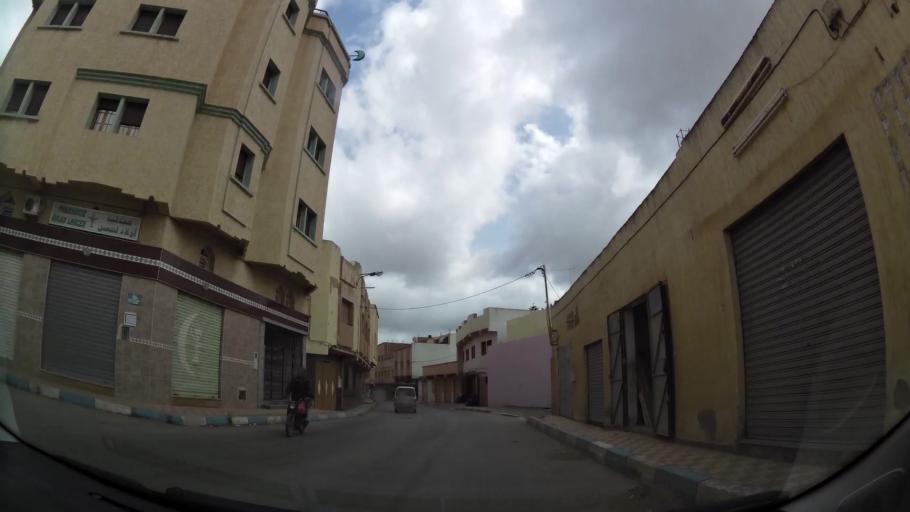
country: MA
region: Oriental
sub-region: Nador
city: Nador
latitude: 35.1629
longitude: -2.9404
